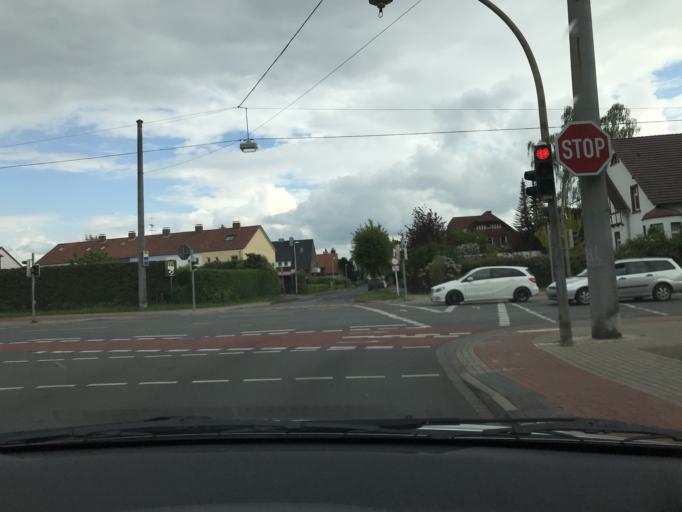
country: DE
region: North Rhine-Westphalia
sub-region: Regierungsbezirk Detmold
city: Minden
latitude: 52.2763
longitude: 8.8976
